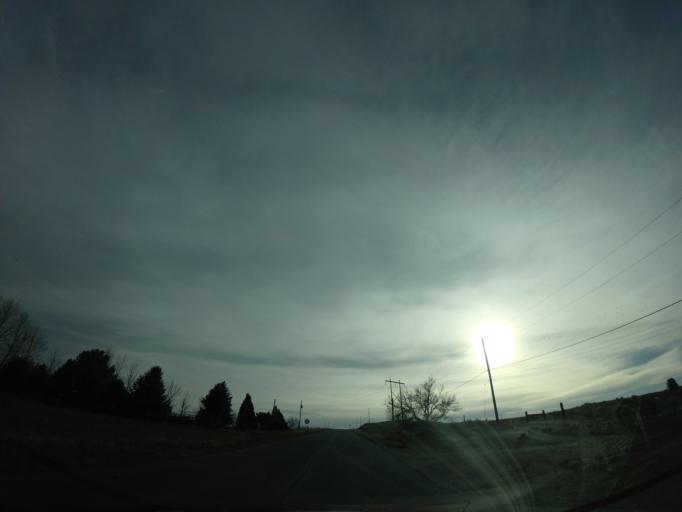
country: US
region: Montana
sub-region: Yellowstone County
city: Billings
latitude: 45.7938
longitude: -108.4555
